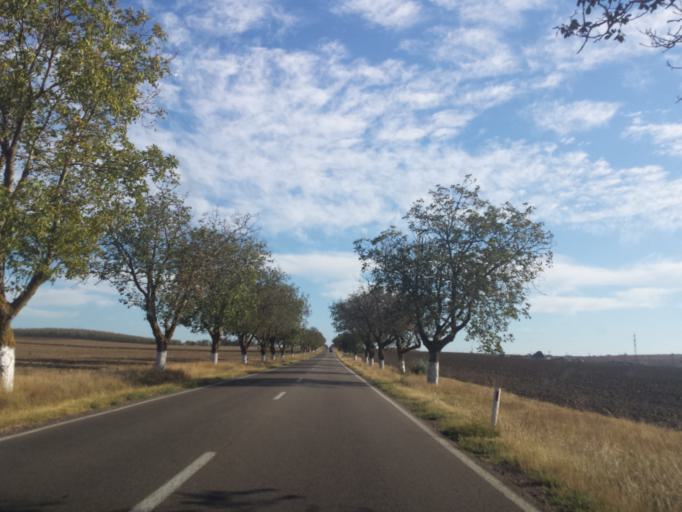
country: RO
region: Tulcea
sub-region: Comuna Frecatei
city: Cataloi
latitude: 45.1237
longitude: 28.7522
